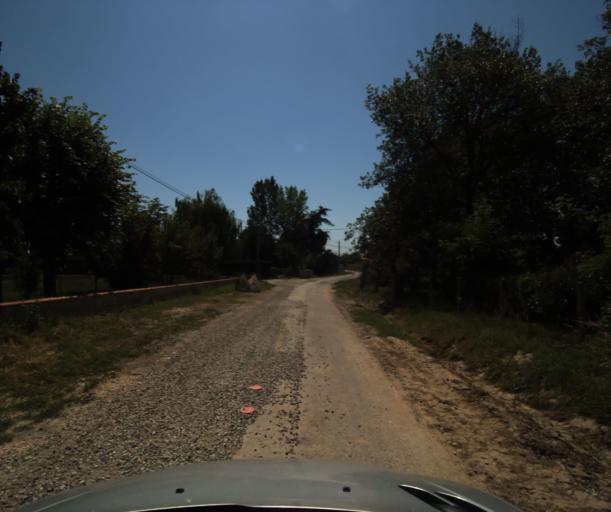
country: FR
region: Midi-Pyrenees
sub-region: Departement de la Haute-Garonne
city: Saubens
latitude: 43.4747
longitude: 1.3649
